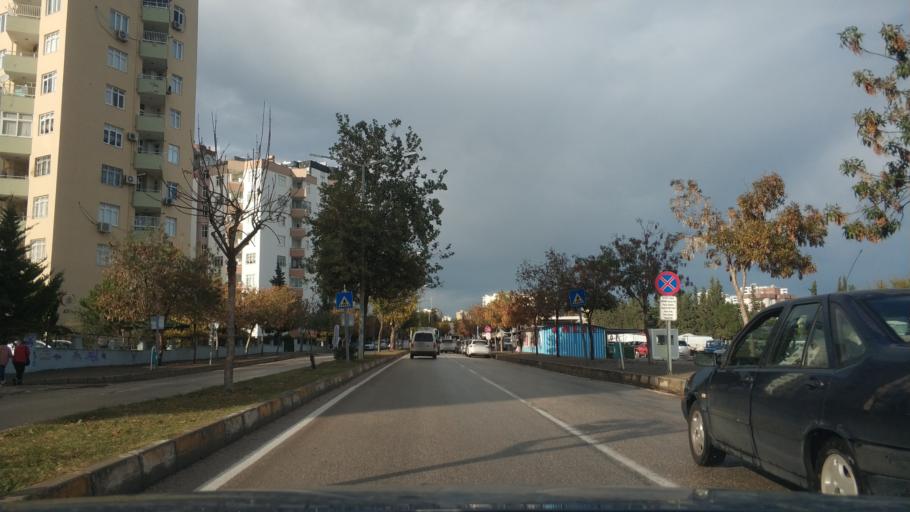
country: TR
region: Adana
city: Seyhan
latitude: 37.0397
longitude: 35.2611
